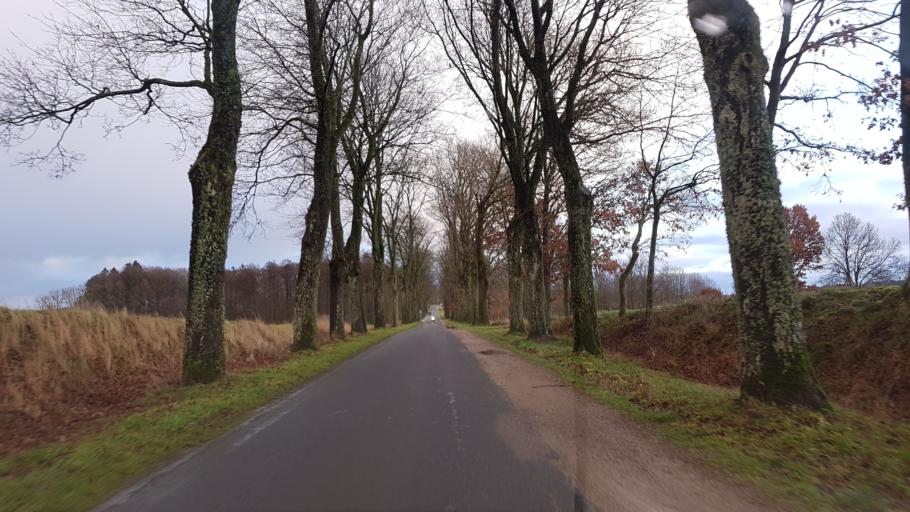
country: PL
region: West Pomeranian Voivodeship
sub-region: Powiat swidwinski
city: Rabino
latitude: 53.9488
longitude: 15.9112
